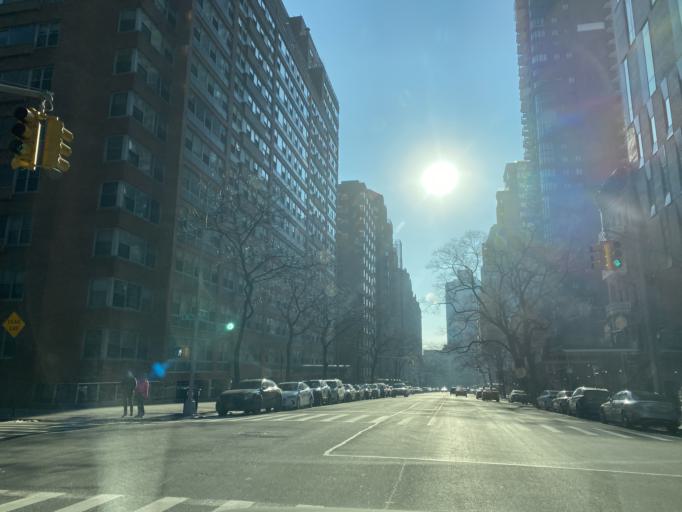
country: US
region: New York
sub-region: New York County
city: Manhattan
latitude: 40.7731
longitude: -73.9461
